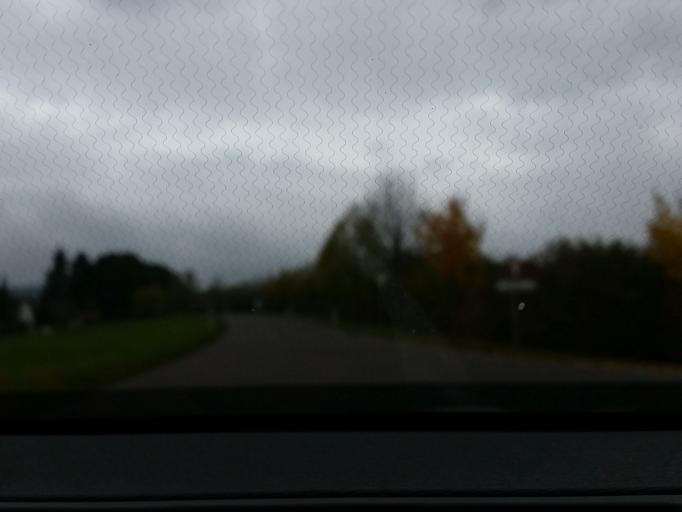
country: DE
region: Saarland
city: Weiskirchen
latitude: 49.5378
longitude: 6.8046
